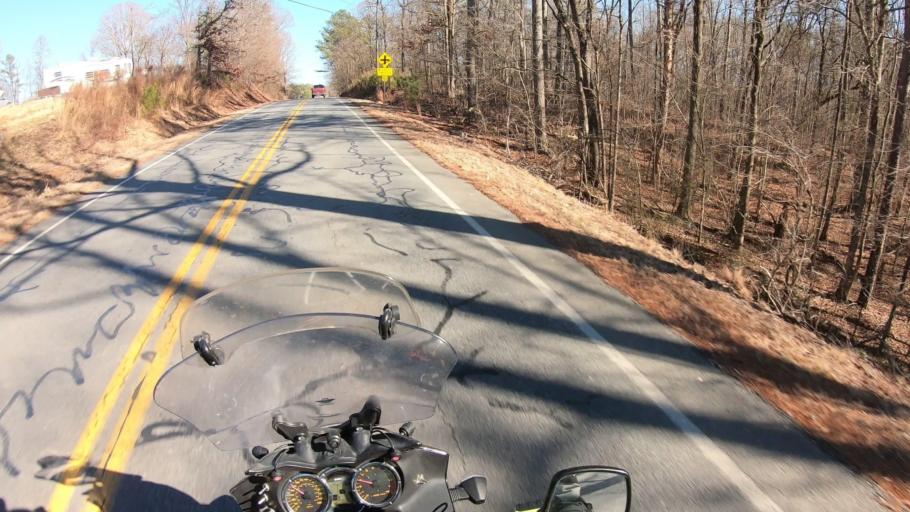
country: US
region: Georgia
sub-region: Gilmer County
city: Ellijay
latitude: 34.6409
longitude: -84.5649
